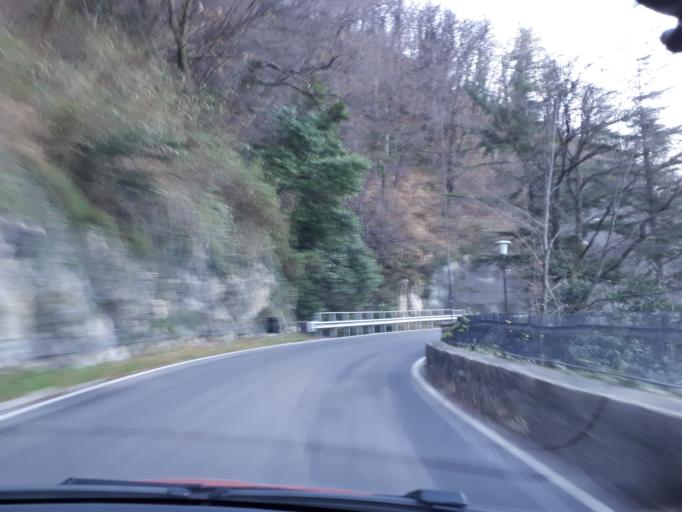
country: IT
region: Lombardy
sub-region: Provincia di Como
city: Nesso
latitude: 45.9313
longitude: 9.1510
